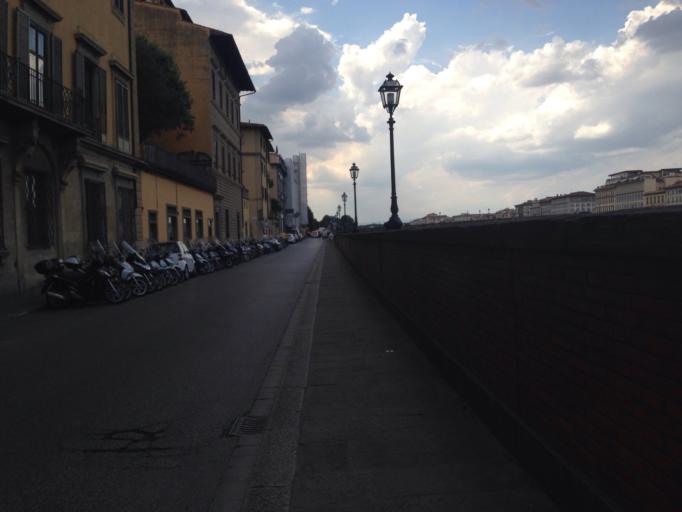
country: IT
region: Tuscany
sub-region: Province of Florence
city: Florence
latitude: 43.7689
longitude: 11.2491
